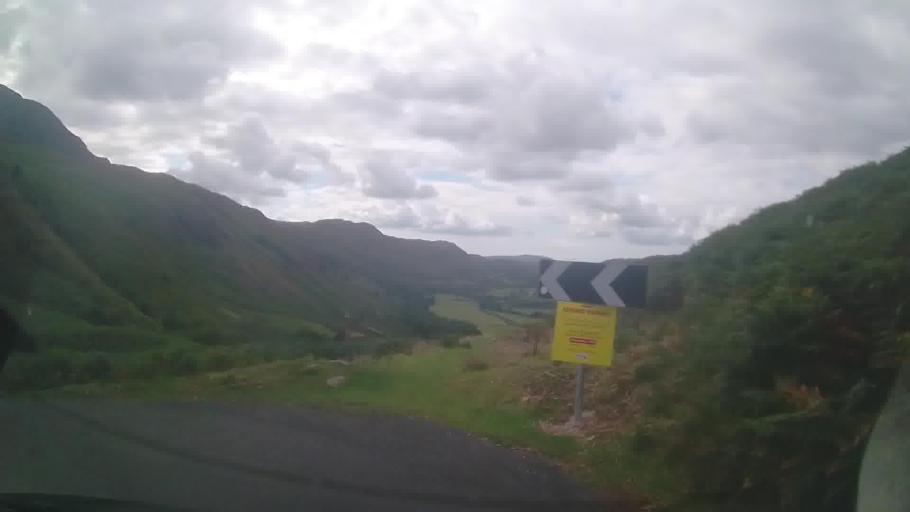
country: GB
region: England
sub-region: Cumbria
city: Millom
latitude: 54.4008
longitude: -3.2070
